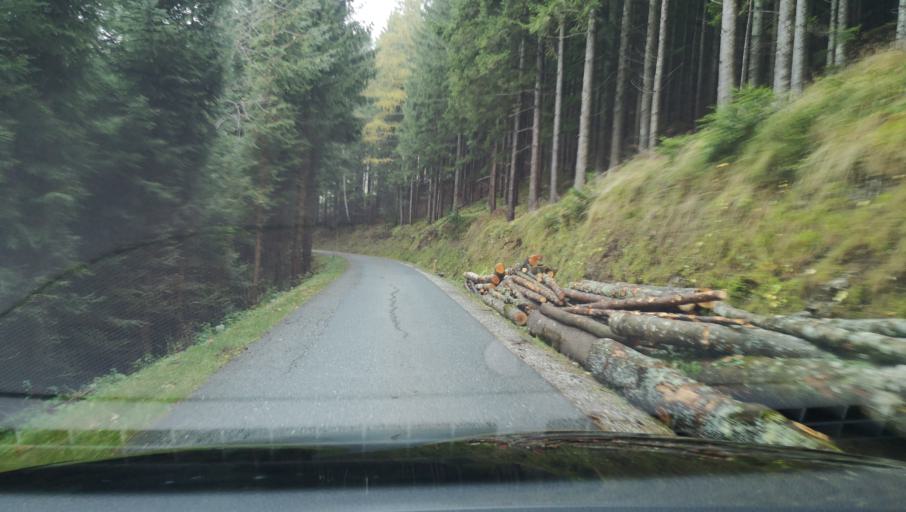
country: AT
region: Styria
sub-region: Politischer Bezirk Weiz
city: Birkfeld
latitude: 47.3442
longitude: 15.6238
